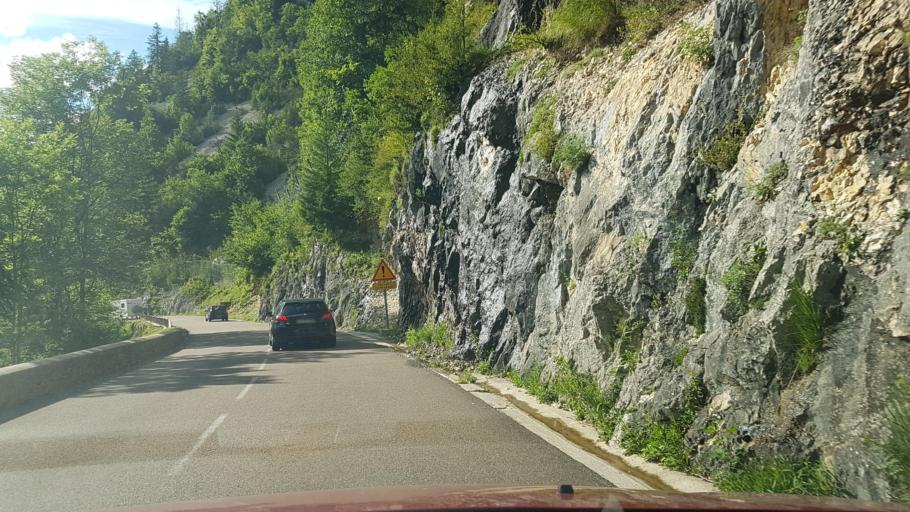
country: FR
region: Franche-Comte
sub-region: Departement du Jura
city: Saint-Claude
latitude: 46.3588
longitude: 5.9008
